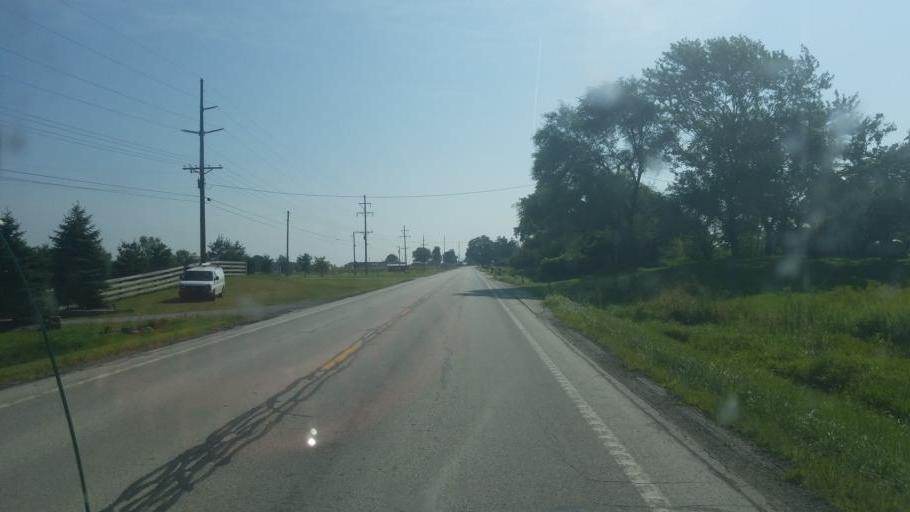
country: US
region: Ohio
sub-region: Wayne County
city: West Salem
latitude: 41.0279
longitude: -82.1788
